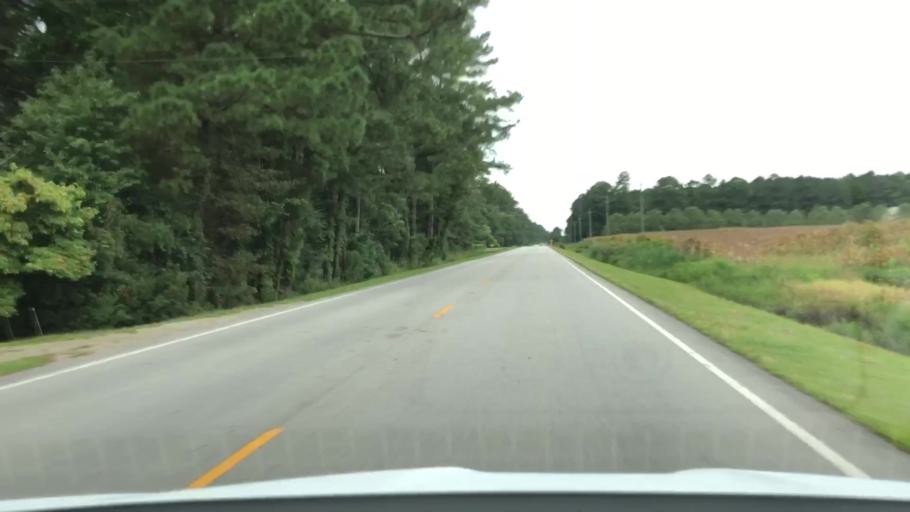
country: US
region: North Carolina
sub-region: Jones County
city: Trenton
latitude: 35.0713
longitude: -77.3767
